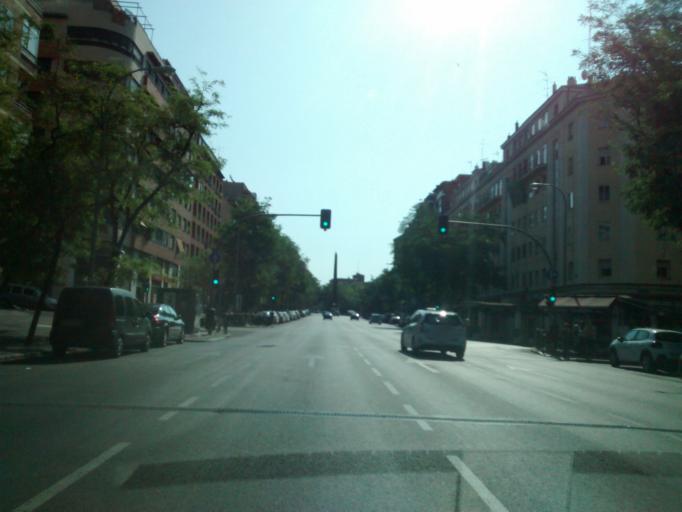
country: ES
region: Madrid
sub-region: Provincia de Madrid
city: Arganzuela
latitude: 40.4010
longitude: -3.6967
